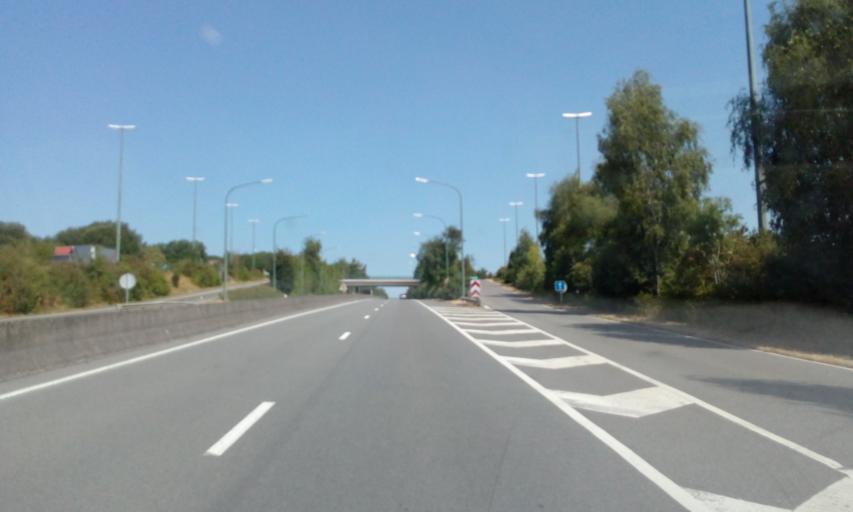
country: BE
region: Wallonia
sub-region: Province du Luxembourg
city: Messancy
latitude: 49.5851
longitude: 5.8089
